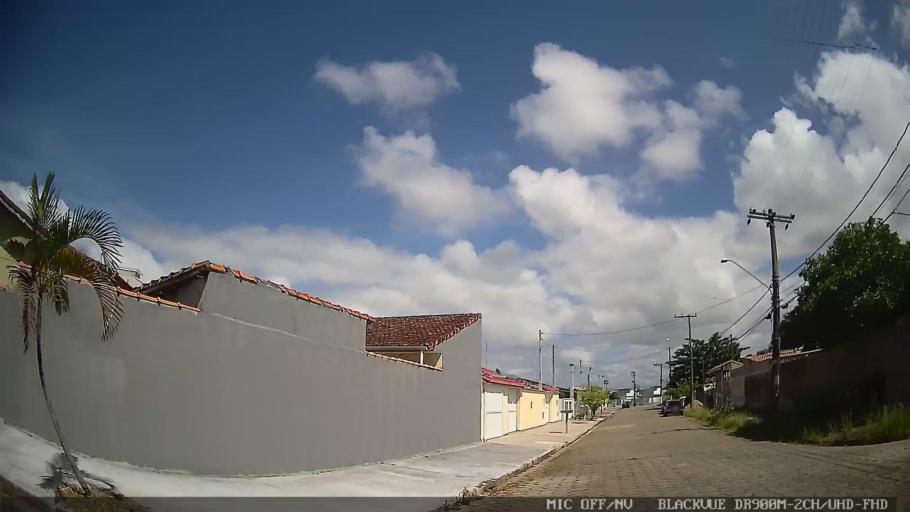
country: BR
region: Sao Paulo
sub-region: Peruibe
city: Peruibe
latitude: -24.3092
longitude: -47.0045
